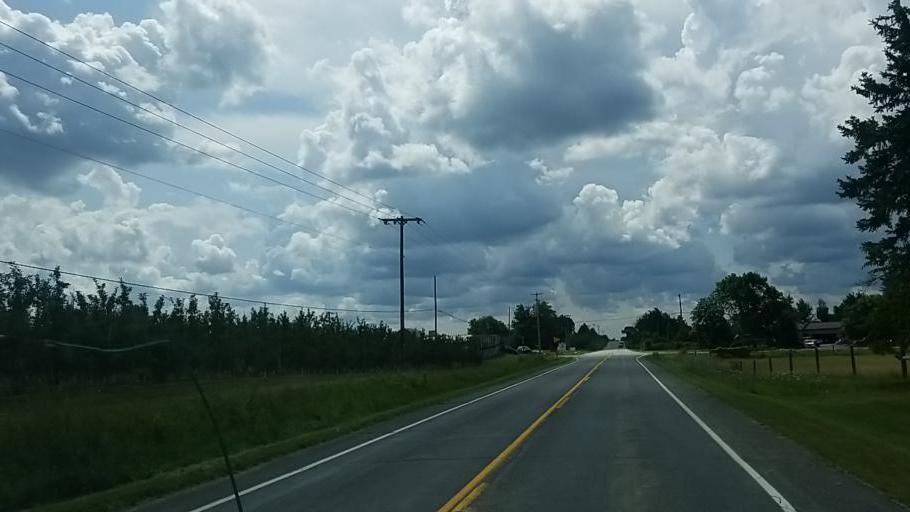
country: US
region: Michigan
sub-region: Kent County
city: Walker
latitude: 43.0898
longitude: -85.7681
